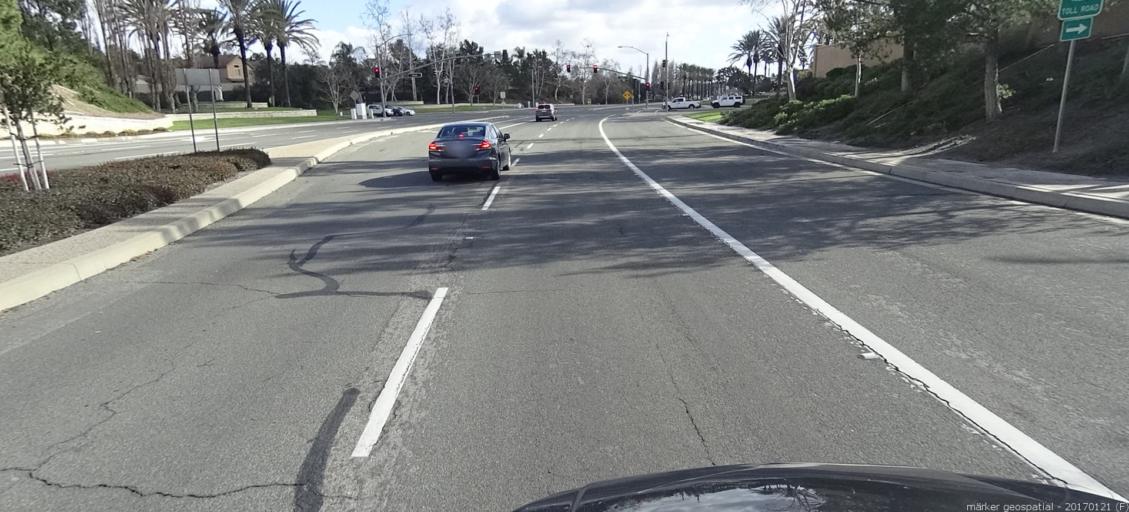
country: US
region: California
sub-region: Orange County
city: Foothill Ranch
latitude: 33.6840
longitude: -117.6674
